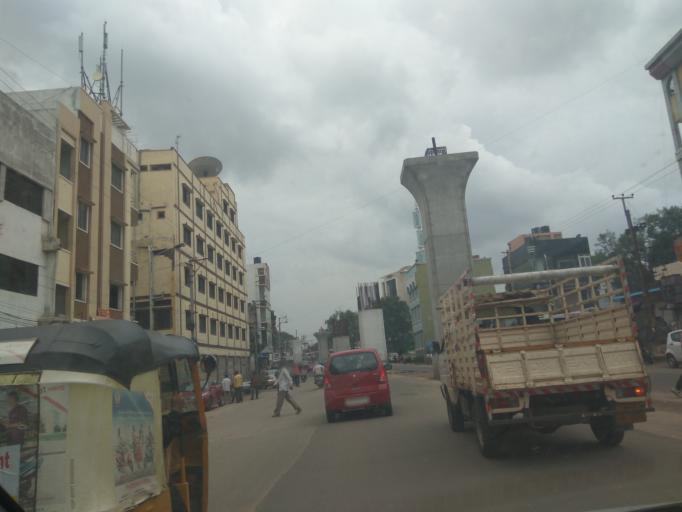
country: IN
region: Telangana
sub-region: Hyderabad
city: Malkajgiri
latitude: 17.4147
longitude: 78.4980
